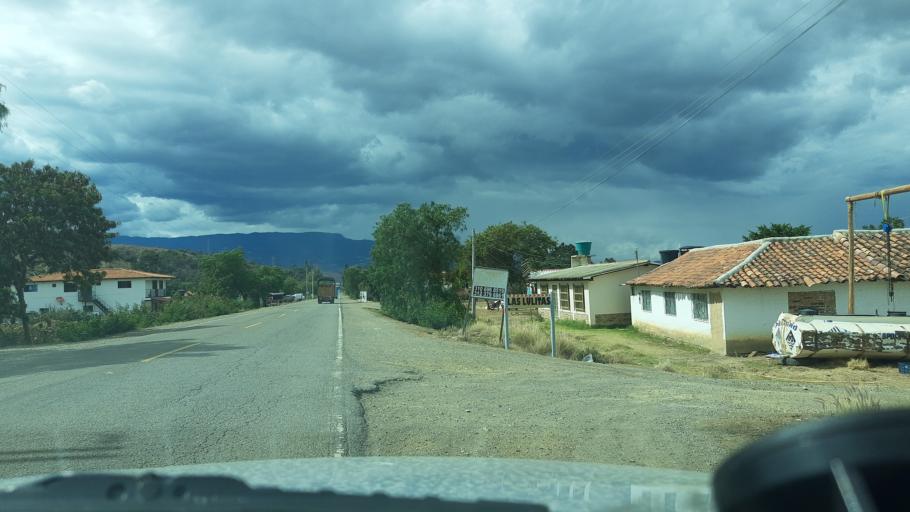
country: CO
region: Boyaca
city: Sachica
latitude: 5.5929
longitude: -73.5452
